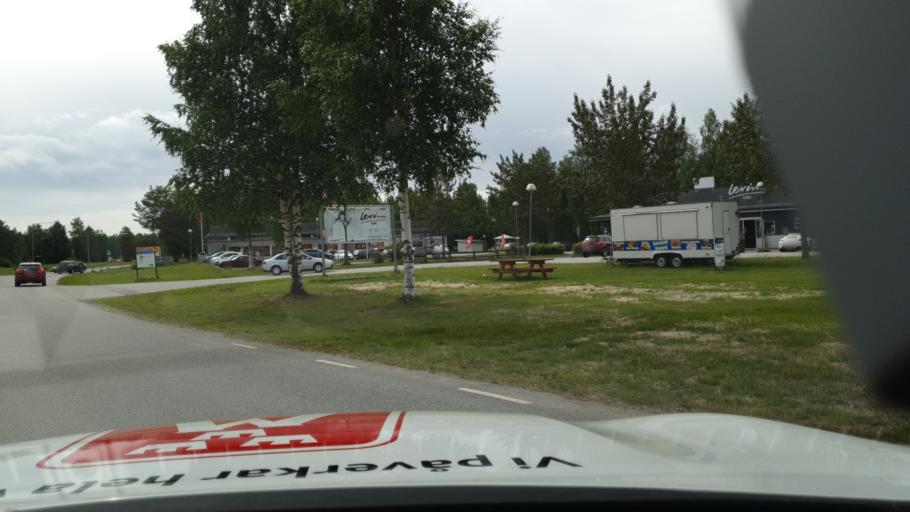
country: SE
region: Vaesterbotten
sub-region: Nordmalings Kommun
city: Nordmaling
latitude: 63.5680
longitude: 19.4949
